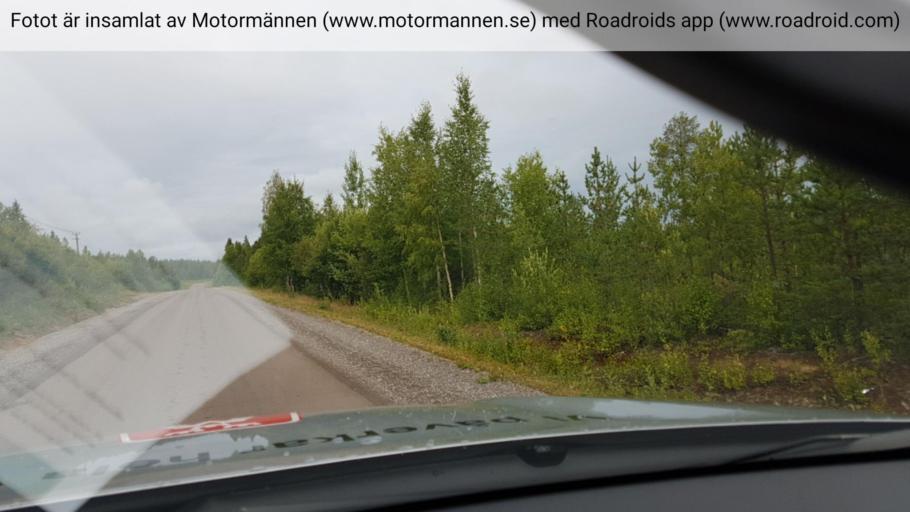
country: SE
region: Norrbotten
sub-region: Alvsbyns Kommun
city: AElvsbyn
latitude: 66.0146
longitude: 21.0481
